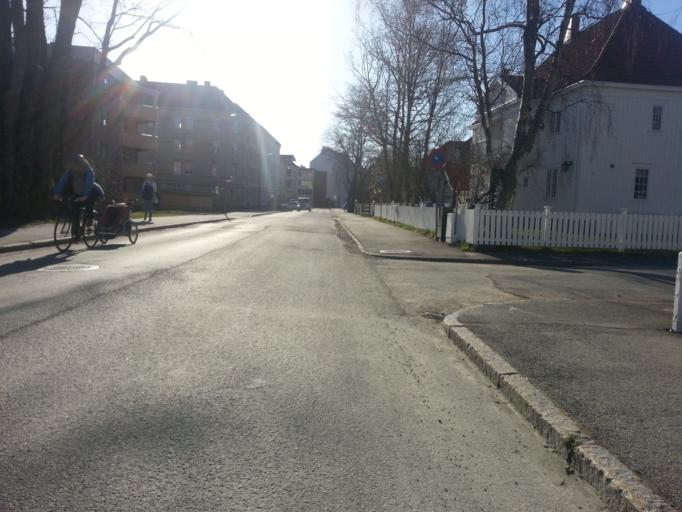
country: NO
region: Sor-Trondelag
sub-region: Trondheim
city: Trondheim
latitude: 63.4254
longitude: 10.3818
